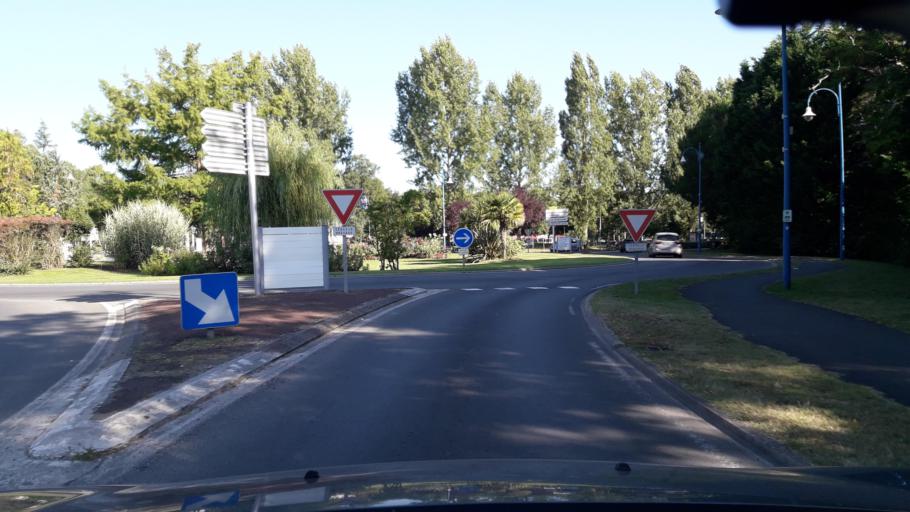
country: FR
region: Poitou-Charentes
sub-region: Departement de la Charente-Maritime
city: Les Mathes
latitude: 45.7121
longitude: -1.1602
